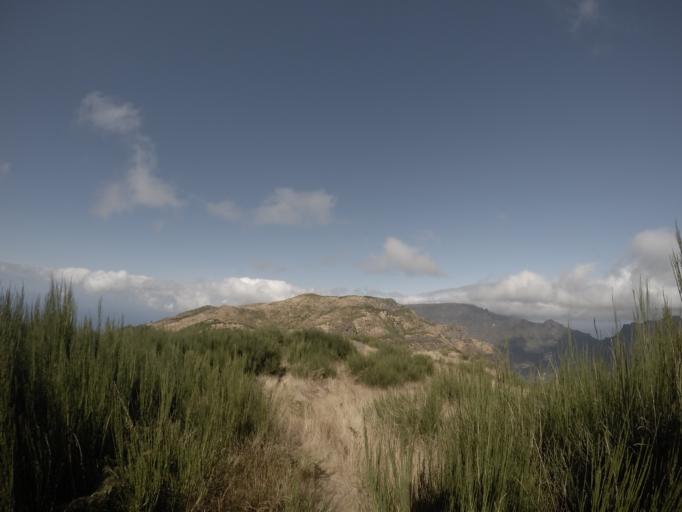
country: PT
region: Madeira
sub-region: Camara de Lobos
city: Curral das Freiras
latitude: 32.7151
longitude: -16.9930
